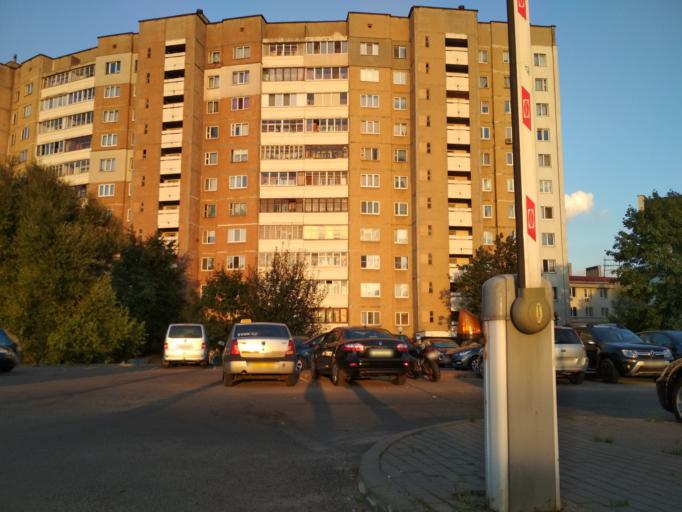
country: BY
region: Minsk
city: Minsk
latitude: 53.8827
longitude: 27.5378
